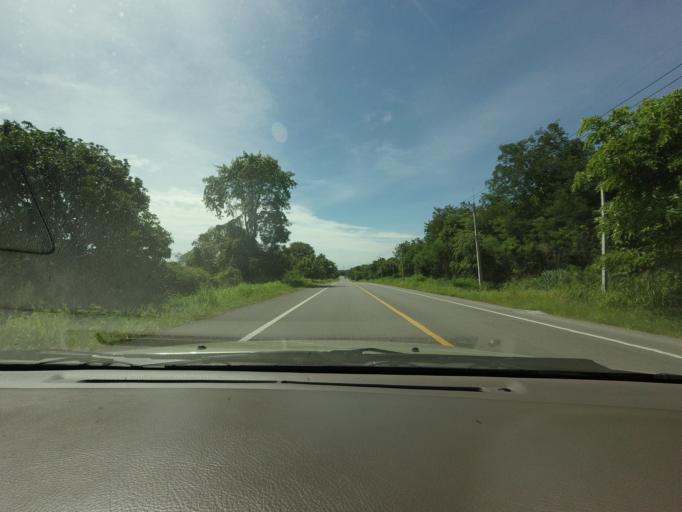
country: TH
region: Chon Buri
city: Si Racha
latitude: 13.2439
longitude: 100.9597
